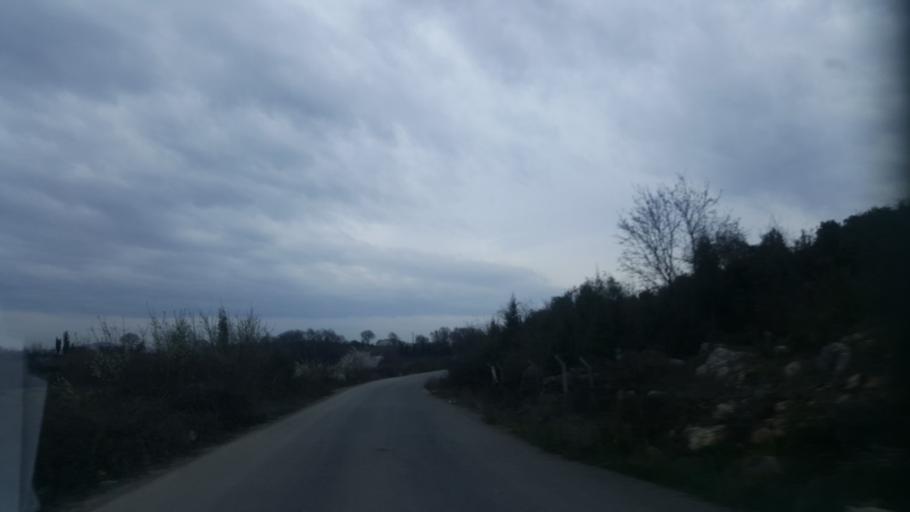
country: TR
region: Kocaeli
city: Tavsanli
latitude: 40.8410
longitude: 29.5533
